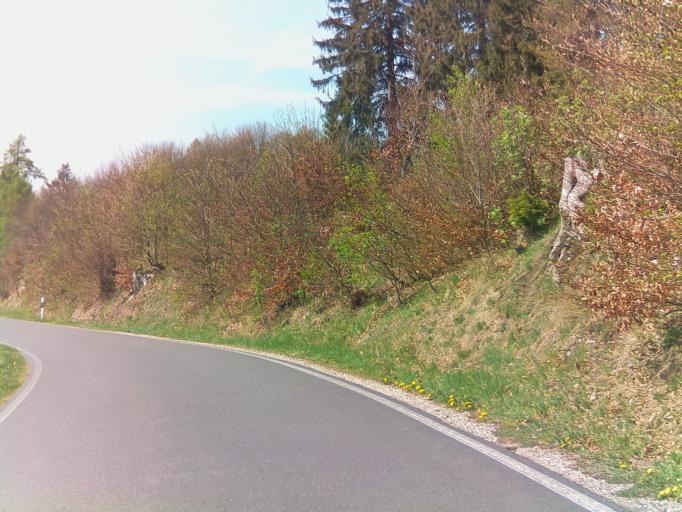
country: DE
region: Thuringia
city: Frauenwald
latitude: 50.5303
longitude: 10.8532
